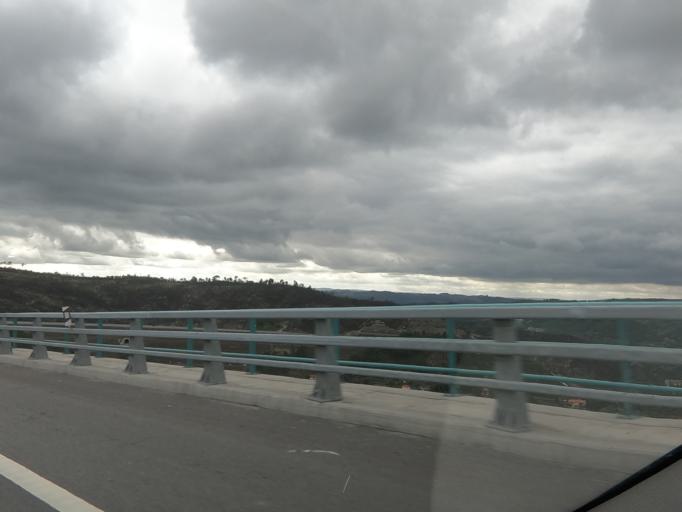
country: PT
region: Porto
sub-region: Baiao
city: Baiao
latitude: 41.2498
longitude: -7.9839
